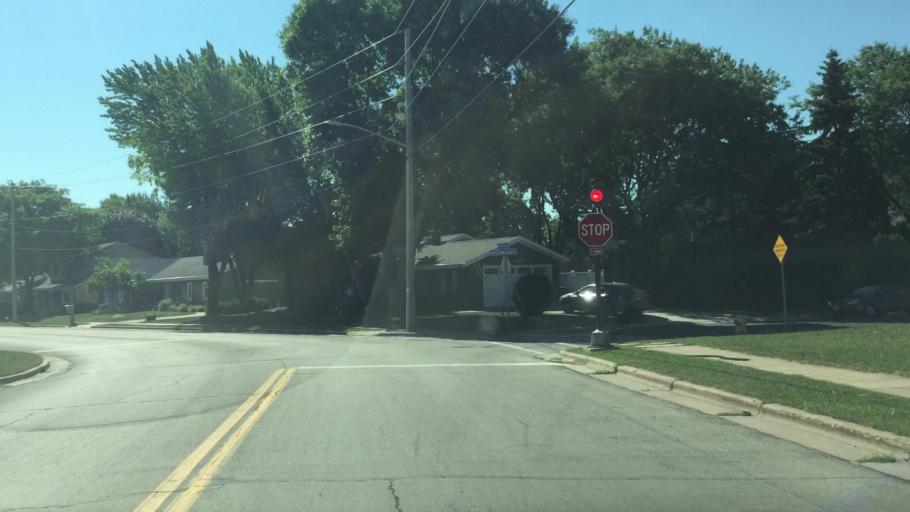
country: US
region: Wisconsin
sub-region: Winnebago County
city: Menasha
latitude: 44.2189
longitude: -88.4198
